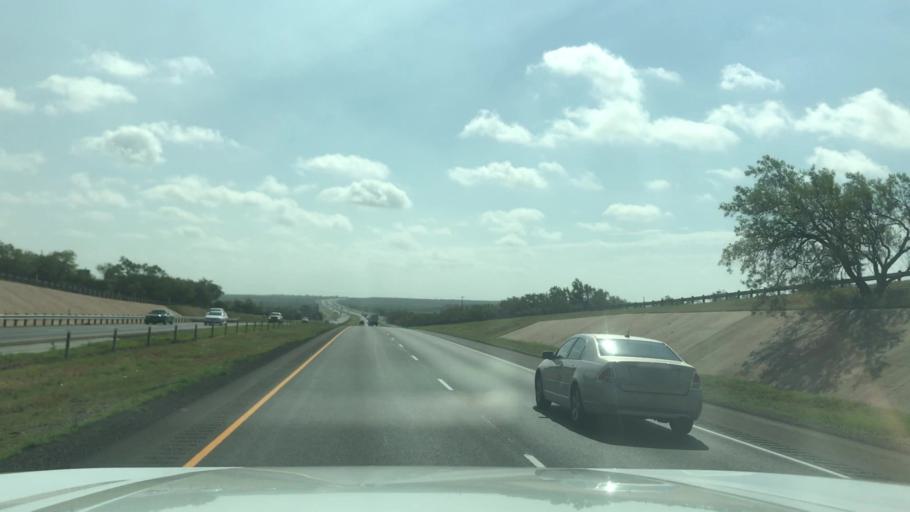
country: US
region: Texas
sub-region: Nolan County
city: Sweetwater
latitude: 32.4941
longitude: -100.3018
